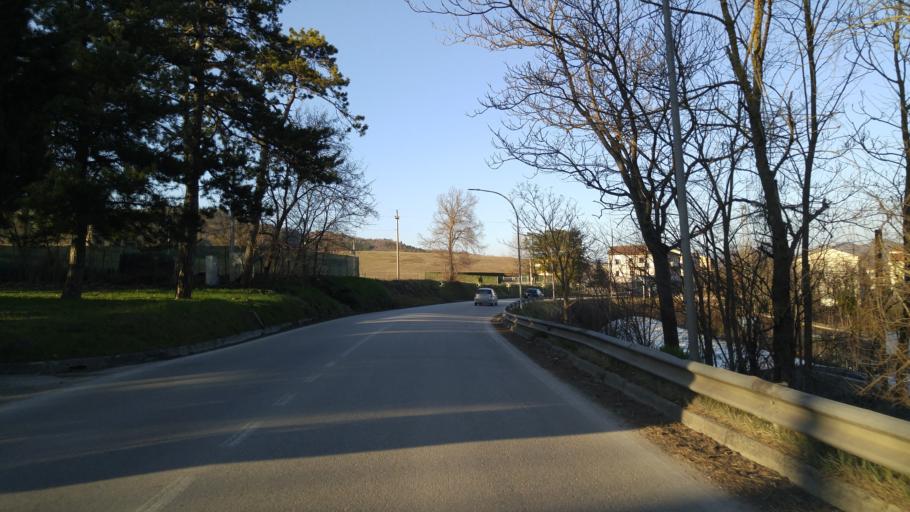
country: IT
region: The Marches
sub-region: Provincia di Pesaro e Urbino
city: Cagli
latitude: 43.5551
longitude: 12.6524
